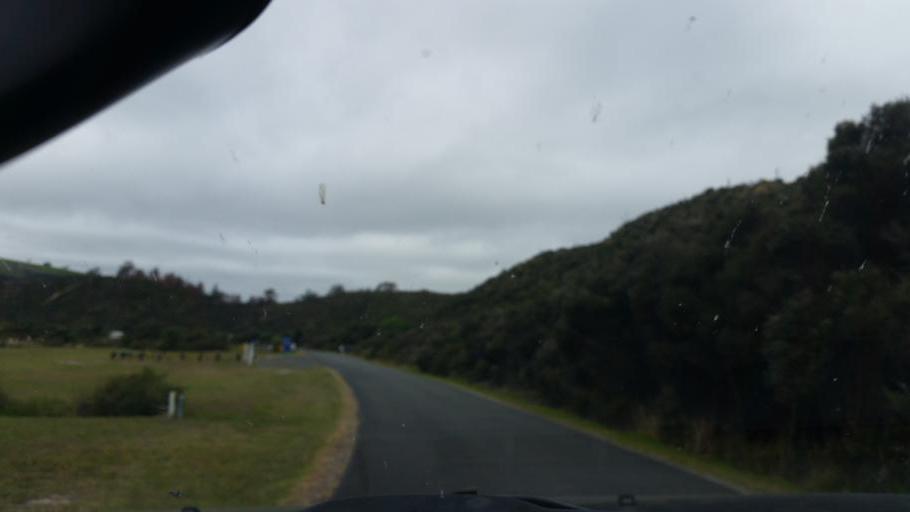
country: NZ
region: Northland
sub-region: Kaipara District
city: Dargaville
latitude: -35.8117
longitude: 173.6609
